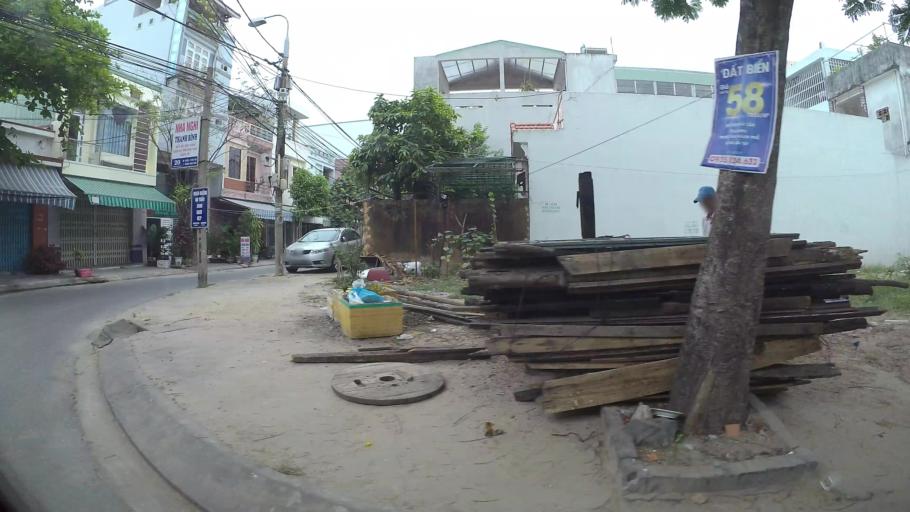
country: VN
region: Da Nang
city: Lien Chieu
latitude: 16.0730
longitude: 108.1728
